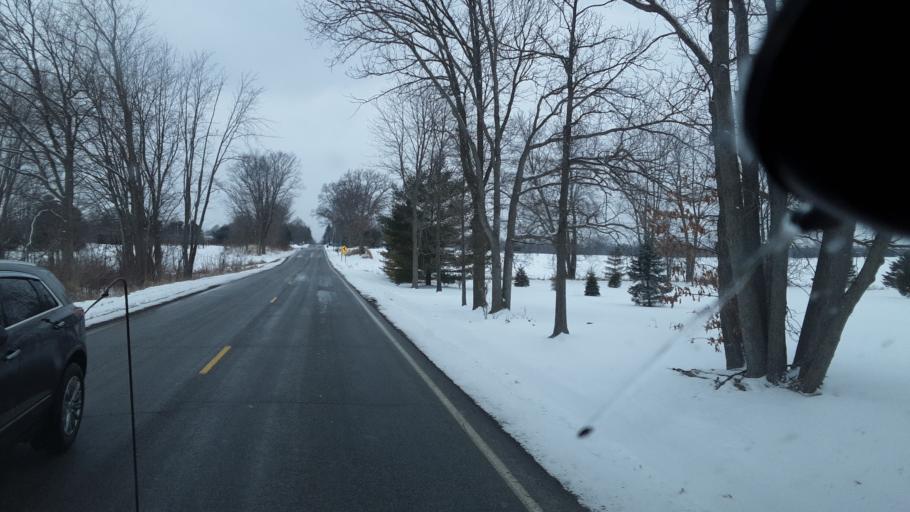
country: US
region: Michigan
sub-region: Ingham County
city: Leslie
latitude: 42.4475
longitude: -84.4102
